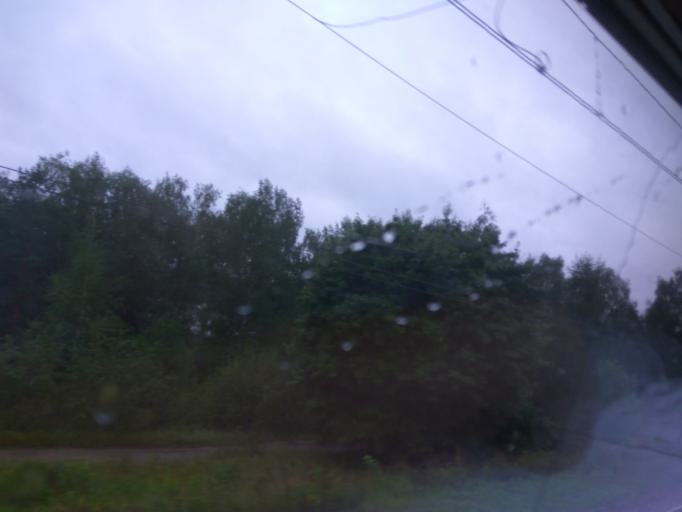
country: RU
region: Moskovskaya
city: Stupino
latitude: 54.8800
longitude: 38.1073
